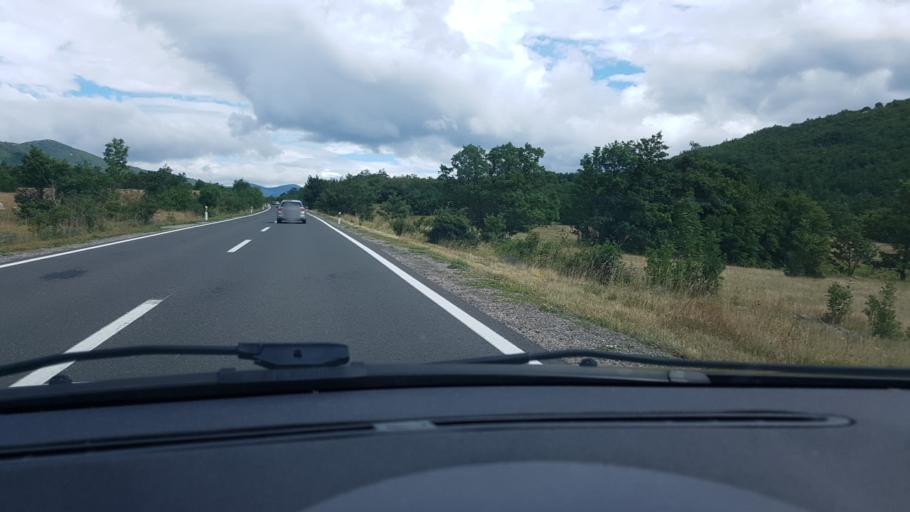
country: HR
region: Zadarska
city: Gracac
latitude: 44.4603
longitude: 15.8114
